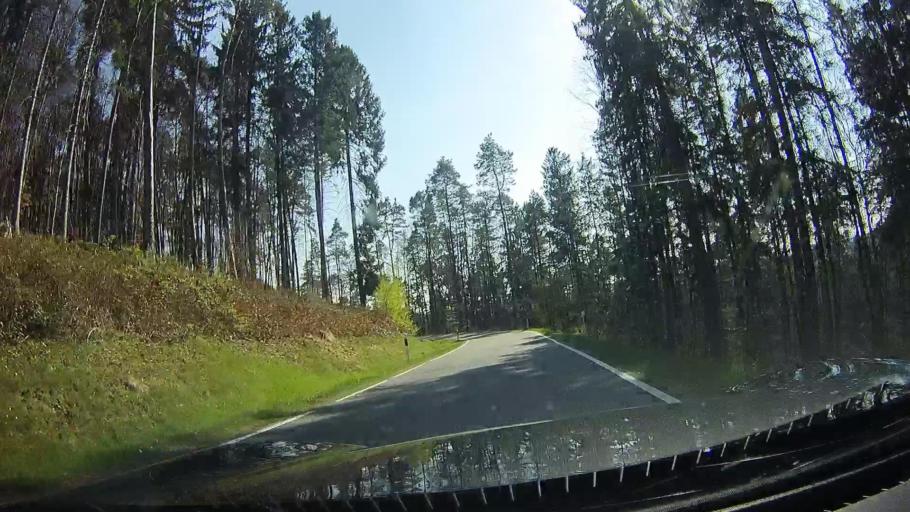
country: DE
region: Hesse
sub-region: Regierungsbezirk Darmstadt
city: Rothenberg
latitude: 49.4887
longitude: 8.9208
